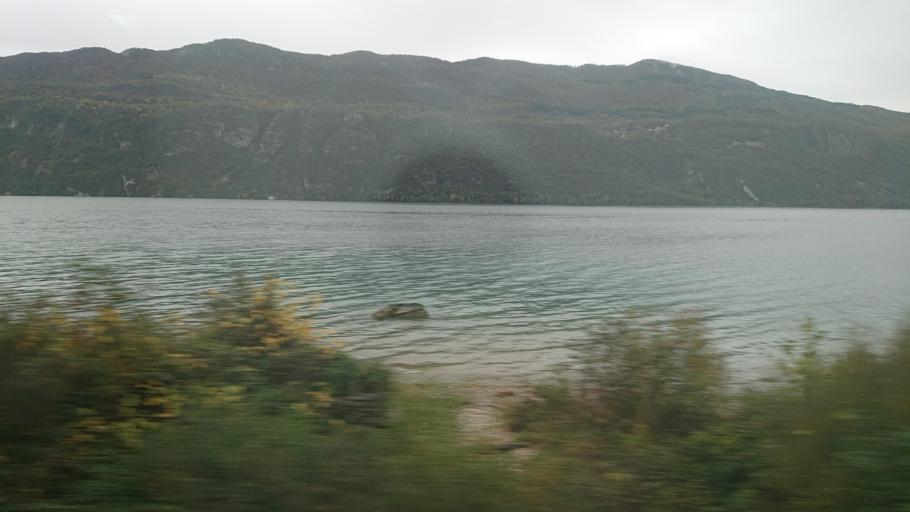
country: FR
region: Rhone-Alpes
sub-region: Departement de la Savoie
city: Brison-Saint-Innocent
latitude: 45.7276
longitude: 5.8801
